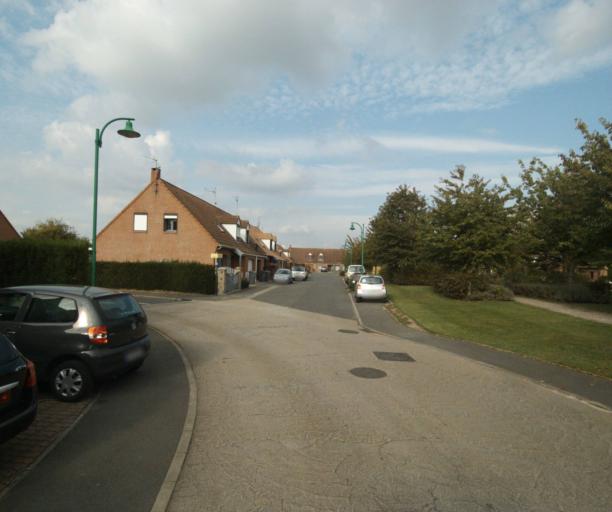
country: FR
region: Nord-Pas-de-Calais
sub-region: Departement du Nord
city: Hallennes-lez-Haubourdin
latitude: 50.6105
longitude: 2.9595
